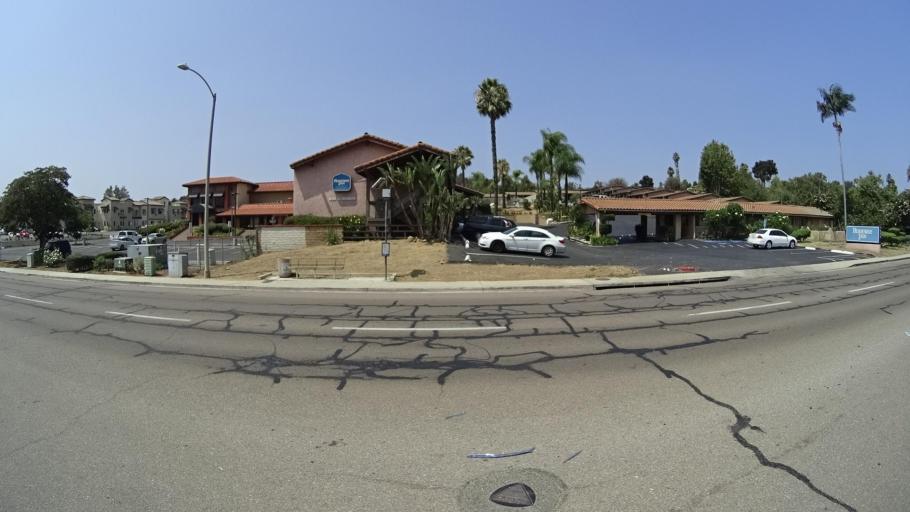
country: US
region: California
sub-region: San Diego County
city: Fallbrook
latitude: 33.3626
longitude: -117.2492
